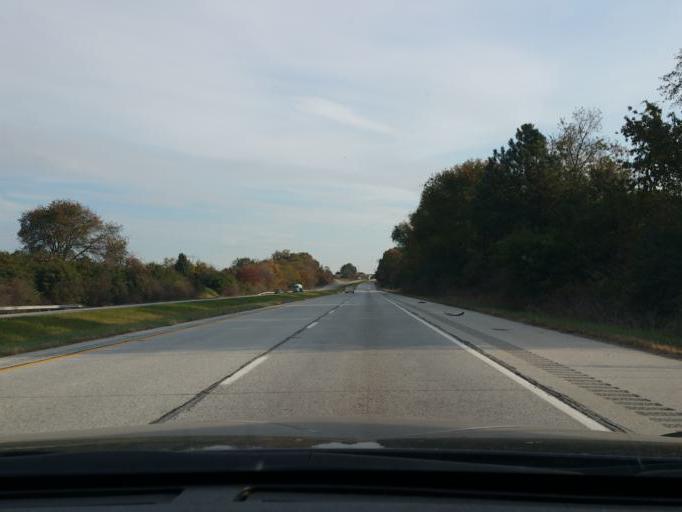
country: US
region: Pennsylvania
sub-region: Chester County
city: Oxford
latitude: 39.7802
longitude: -76.0028
